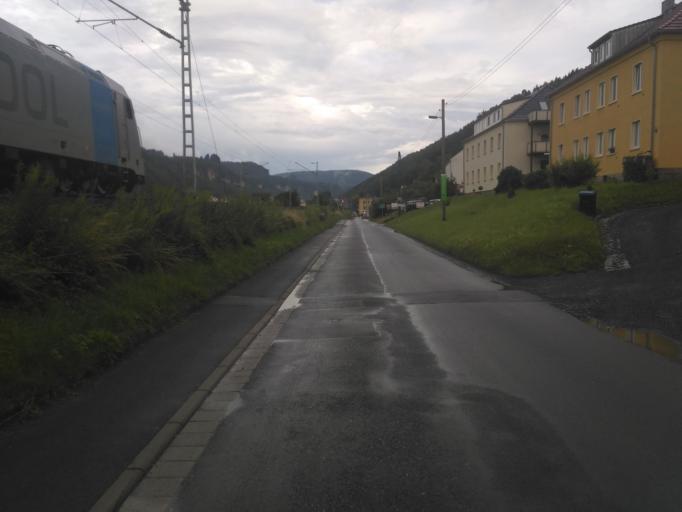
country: DE
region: Saxony
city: Bad Schandau
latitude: 50.9122
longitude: 14.1641
